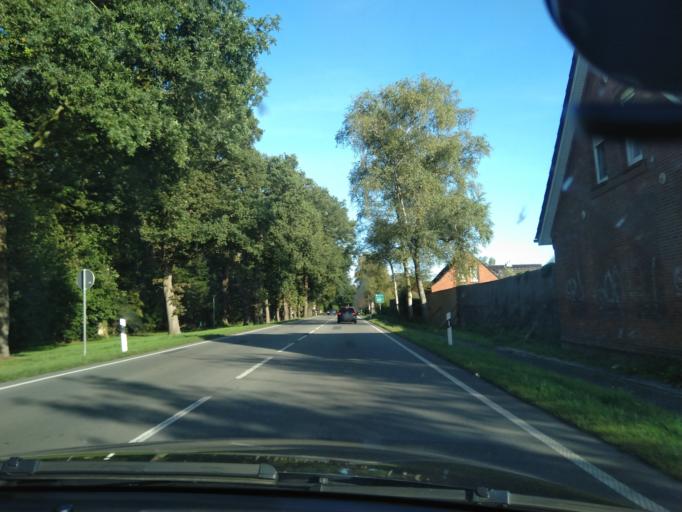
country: DE
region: Lower Saxony
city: Leer
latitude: 53.2375
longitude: 7.4715
